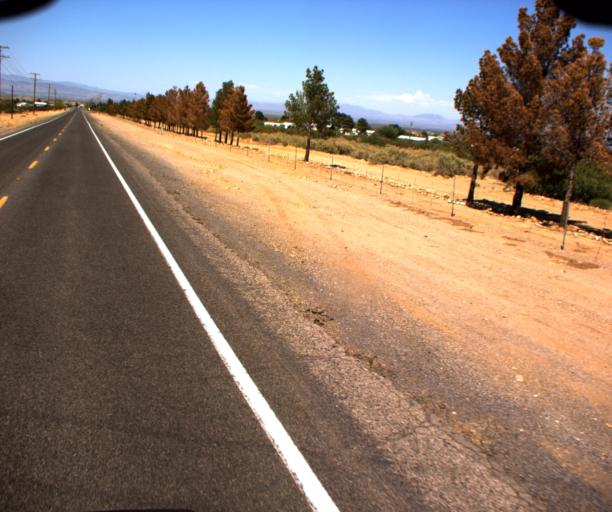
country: US
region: Arizona
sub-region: Graham County
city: Swift Trail Junction
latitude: 32.7206
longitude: -109.7236
